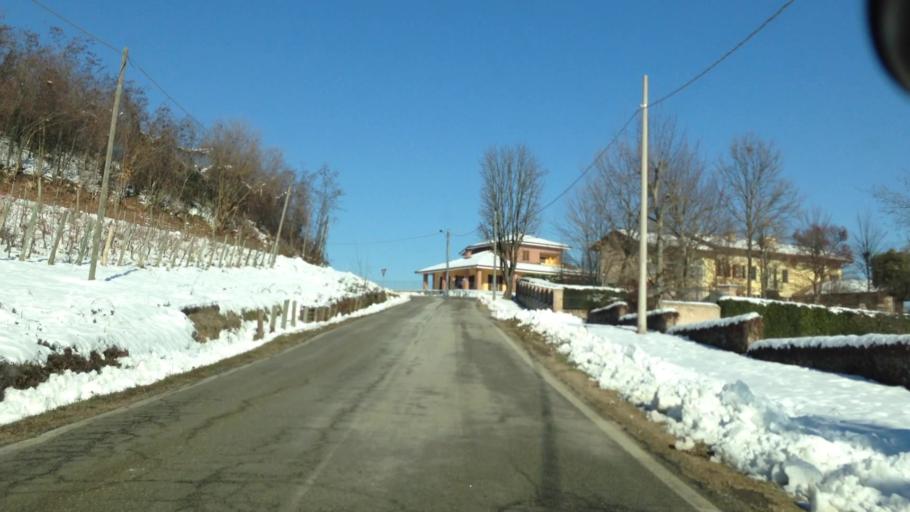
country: IT
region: Piedmont
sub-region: Provincia di Asti
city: Costigliole d'Asti
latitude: 44.7923
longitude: 8.1714
